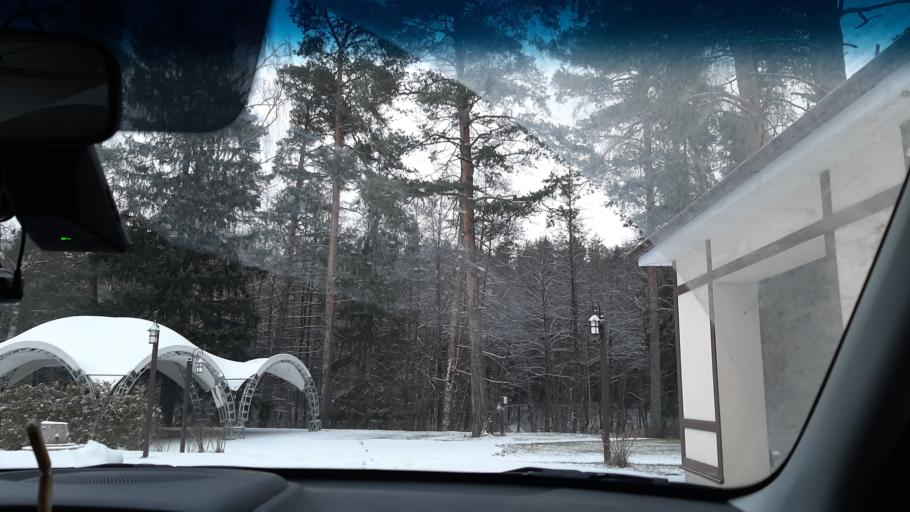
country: RU
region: Ivanovo
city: Kokhma
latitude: 56.8996
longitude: 41.0097
